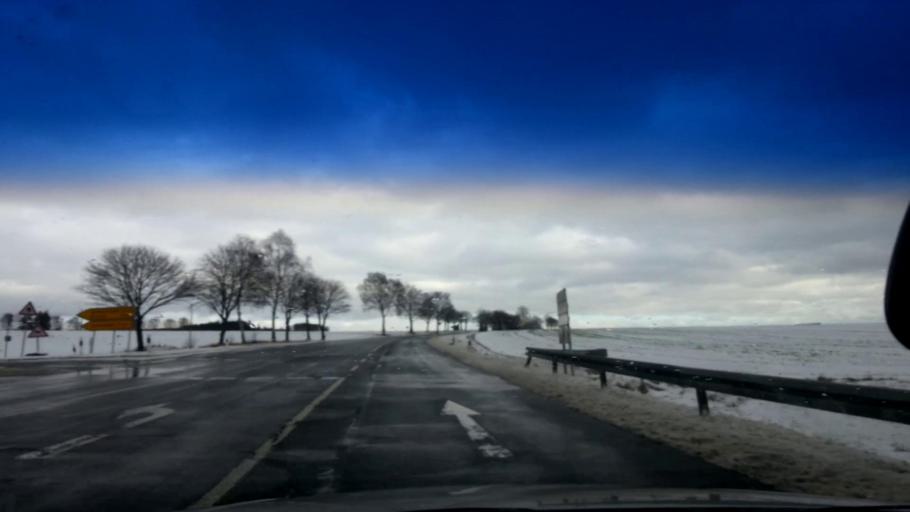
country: DE
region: Bavaria
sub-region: Upper Franconia
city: Schonwald
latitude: 50.1635
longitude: 12.0651
